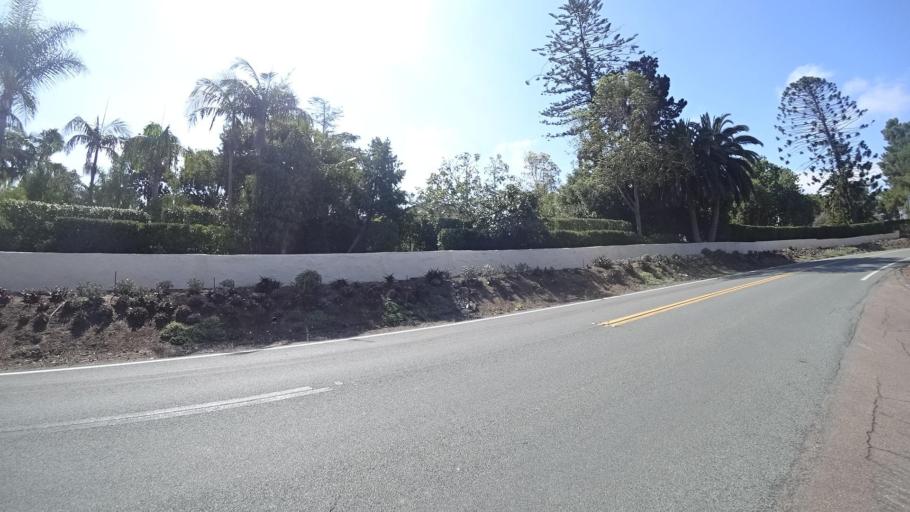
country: US
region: California
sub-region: San Diego County
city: Rancho Santa Fe
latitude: 33.0179
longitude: -117.2103
